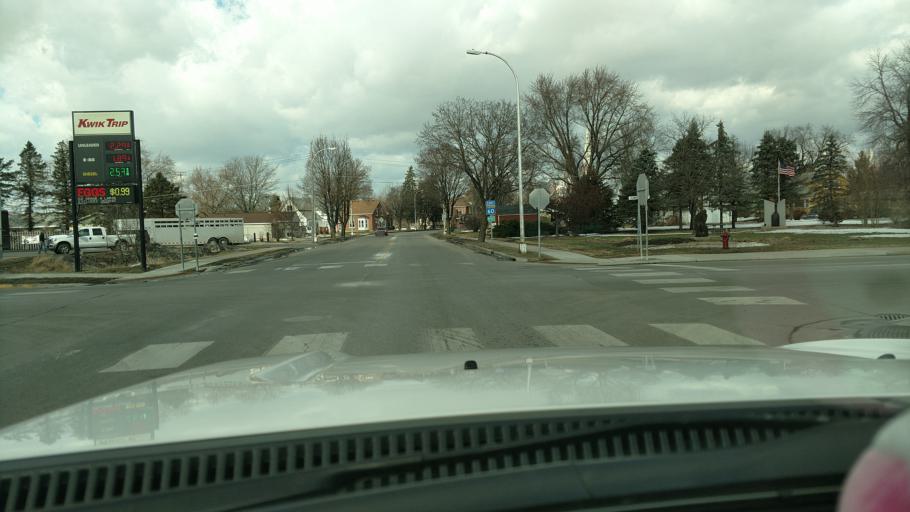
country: US
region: Minnesota
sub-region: Wabasha County
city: Wabasha
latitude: 44.3787
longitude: -92.0347
